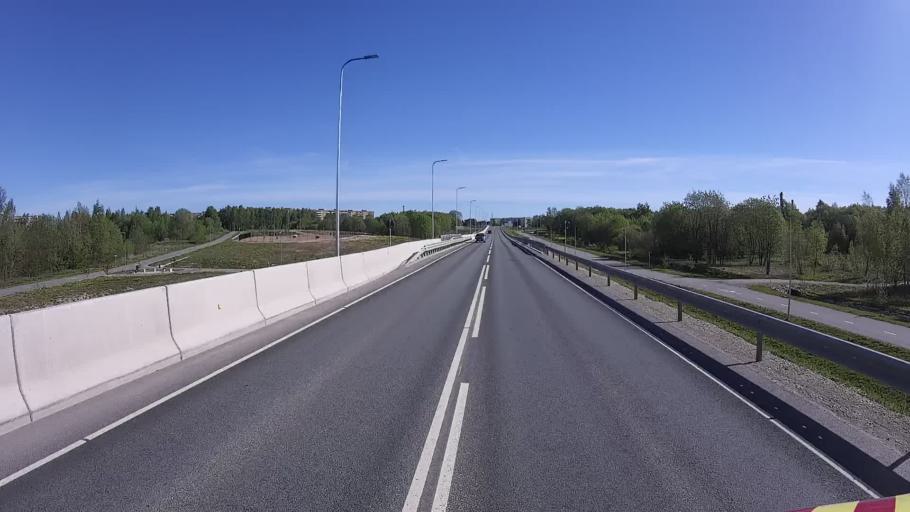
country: EE
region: Tartu
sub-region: Tartu linn
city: Tartu
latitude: 58.3655
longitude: 26.7755
